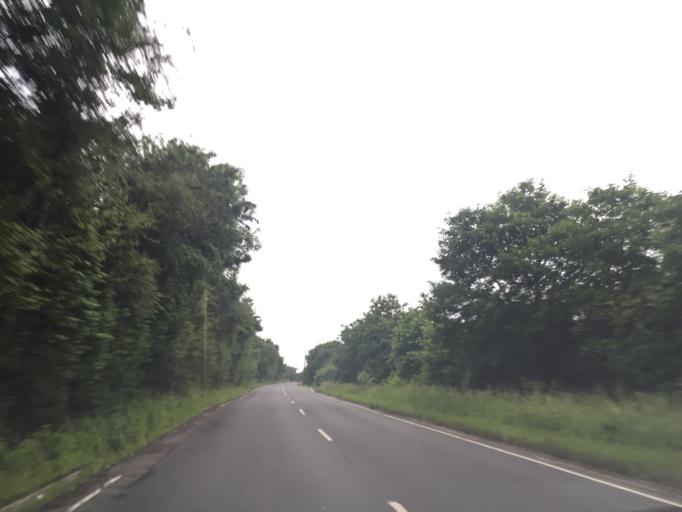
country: GB
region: England
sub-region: Greater London
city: Collier Row
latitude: 51.6347
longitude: 0.1707
